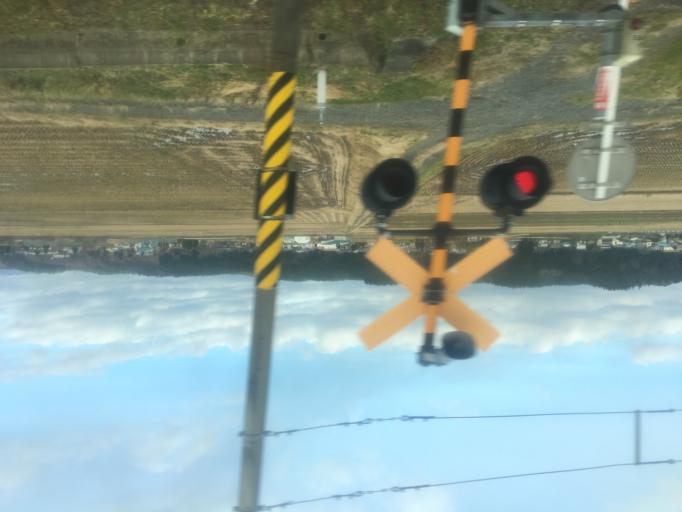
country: JP
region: Akita
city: Takanosu
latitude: 40.2278
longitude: 140.3484
